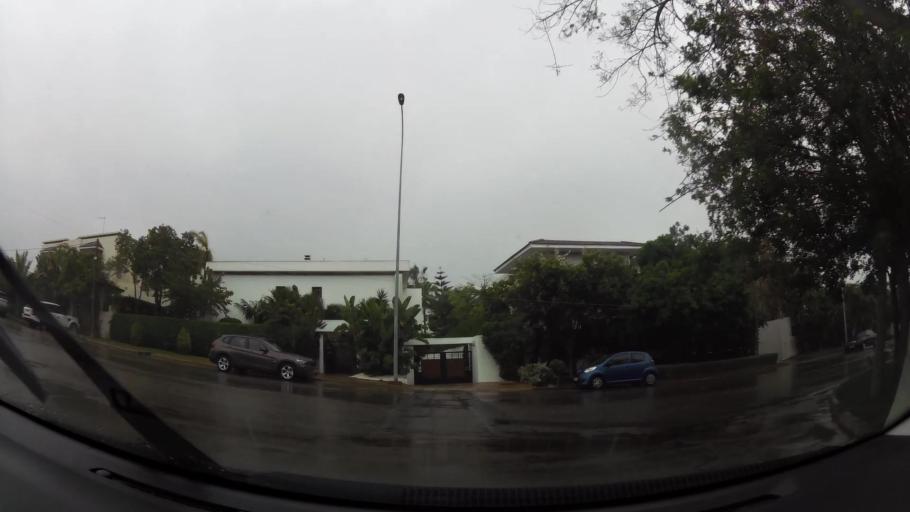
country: MA
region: Grand Casablanca
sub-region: Casablanca
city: Casablanca
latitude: 33.5853
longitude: -7.6769
